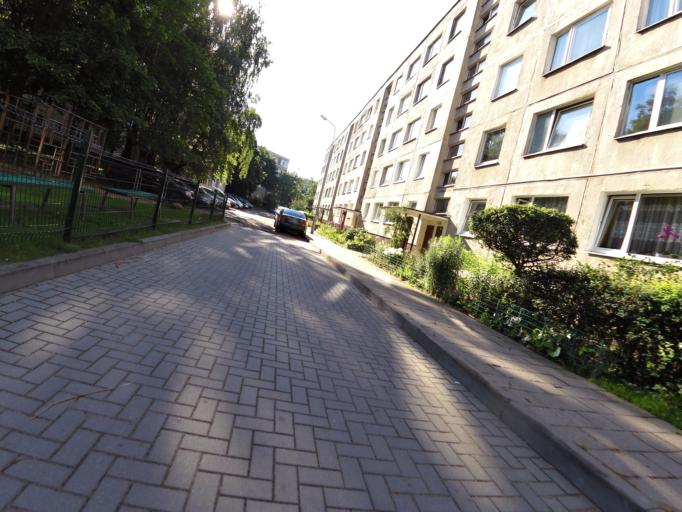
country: LT
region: Vilnius County
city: Justiniskes
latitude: 54.7052
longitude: 25.2299
